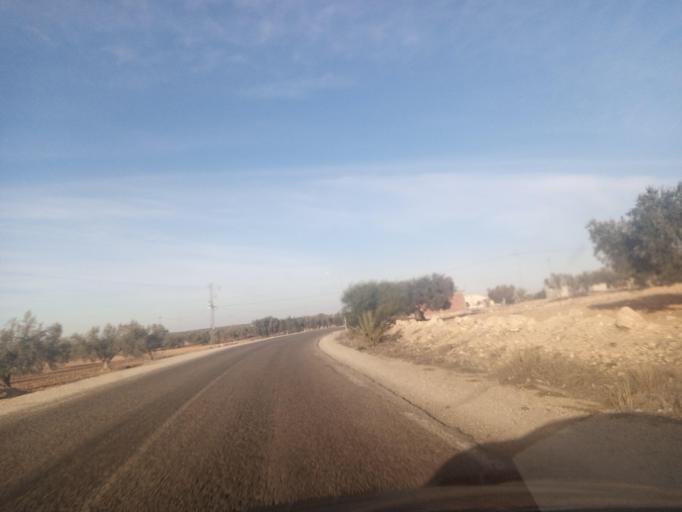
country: TN
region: Al Mahdiyah
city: Shurban
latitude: 34.9554
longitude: 10.3585
